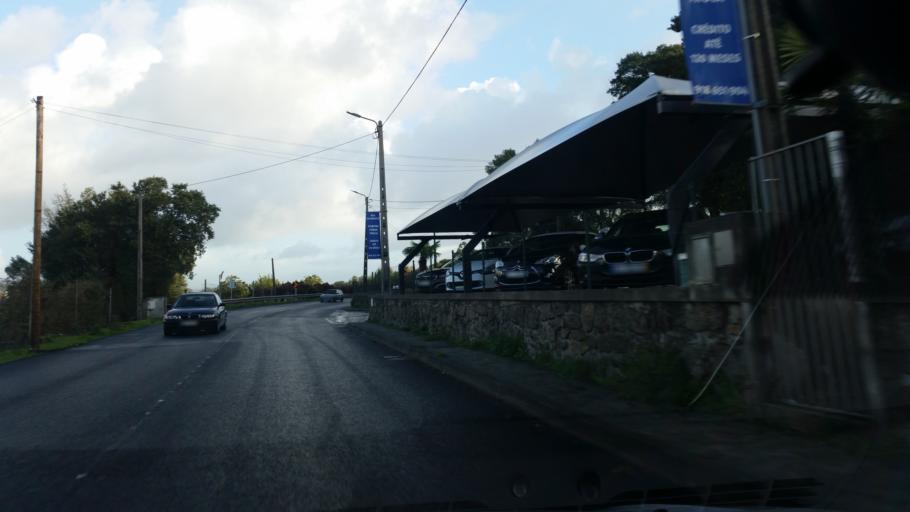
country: PT
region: Porto
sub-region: Santo Tirso
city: Sao Miguel do Couto
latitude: 41.3466
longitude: -8.4623
